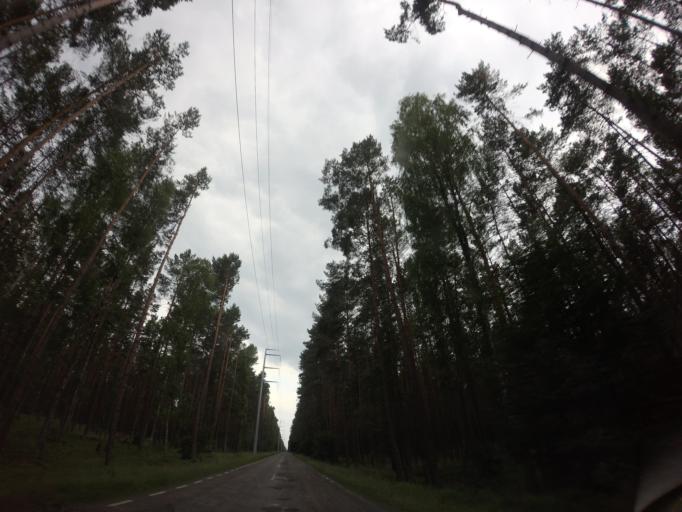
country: PL
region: West Pomeranian Voivodeship
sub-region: Powiat drawski
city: Czaplinek
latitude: 53.4698
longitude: 16.2225
